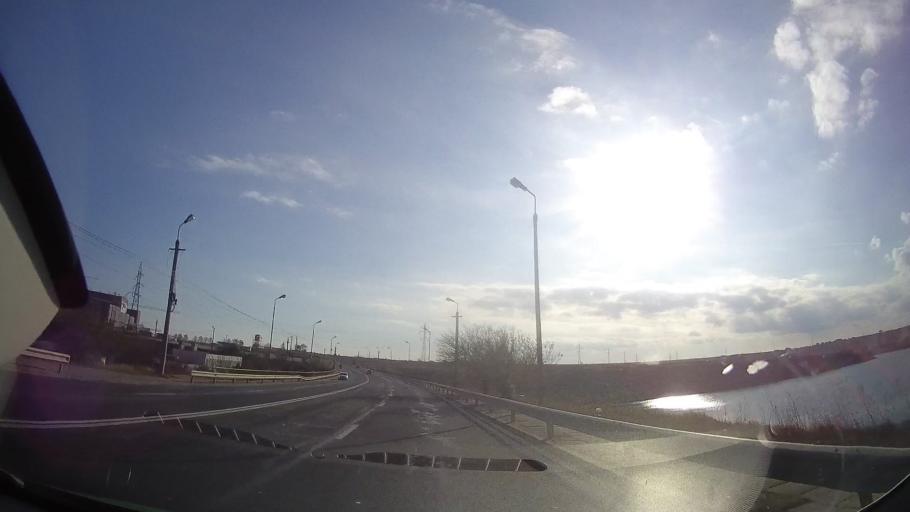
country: RO
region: Constanta
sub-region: Municipiul Mangalia
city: Mangalia
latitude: 43.8011
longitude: 28.5594
